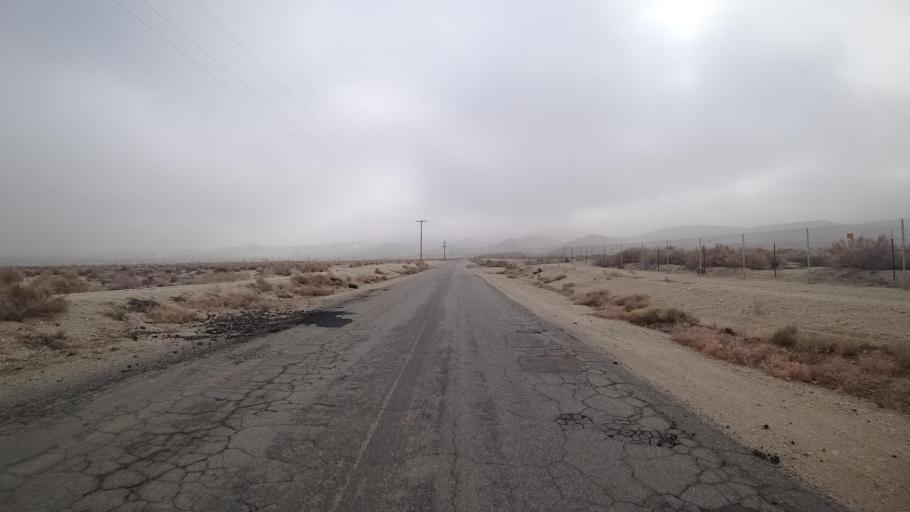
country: US
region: California
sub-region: Kern County
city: Maricopa
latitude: 35.0492
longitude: -119.3925
